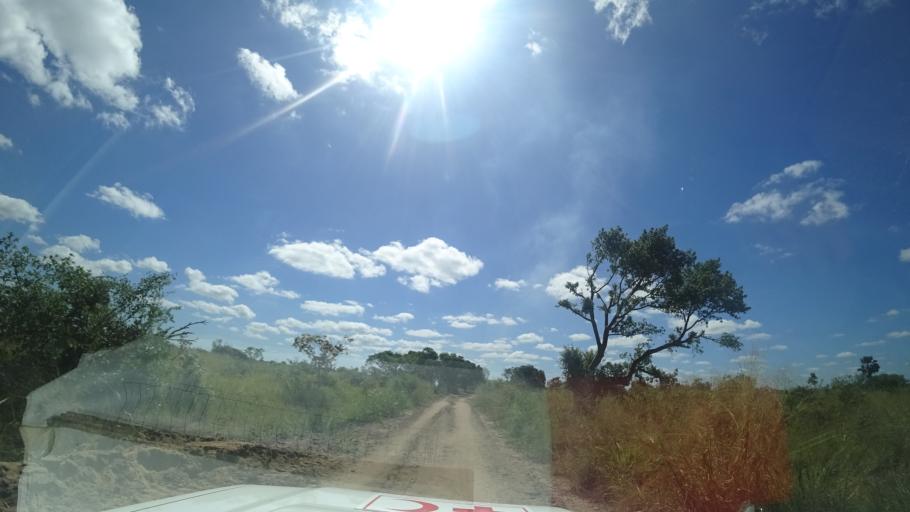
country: MZ
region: Sofala
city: Dondo
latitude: -19.4550
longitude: 34.5949
